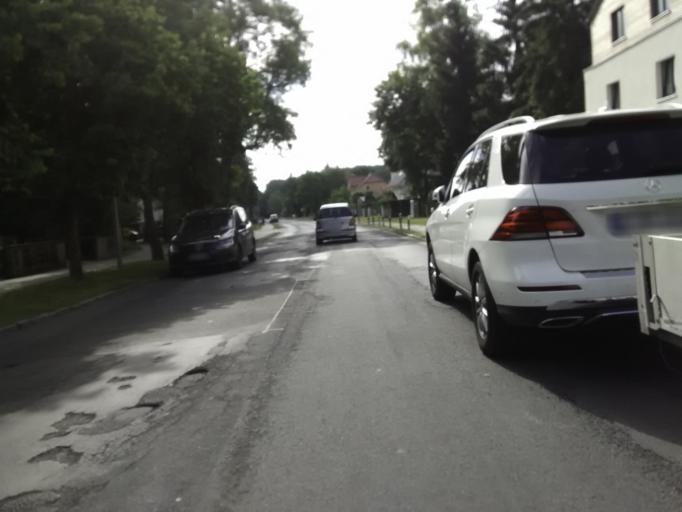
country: DE
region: Brandenburg
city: Birkenwerder
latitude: 52.6643
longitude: 13.3110
